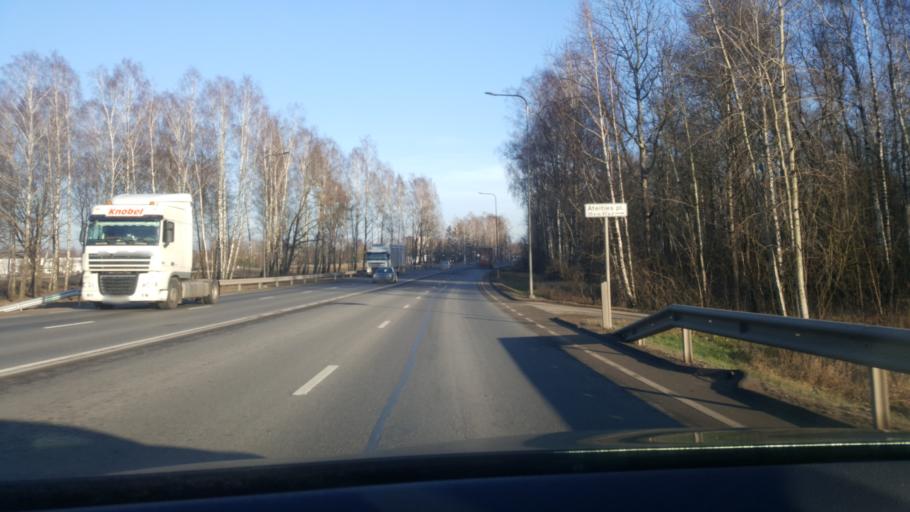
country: LT
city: Ramuciai
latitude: 54.9143
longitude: 24.0365
